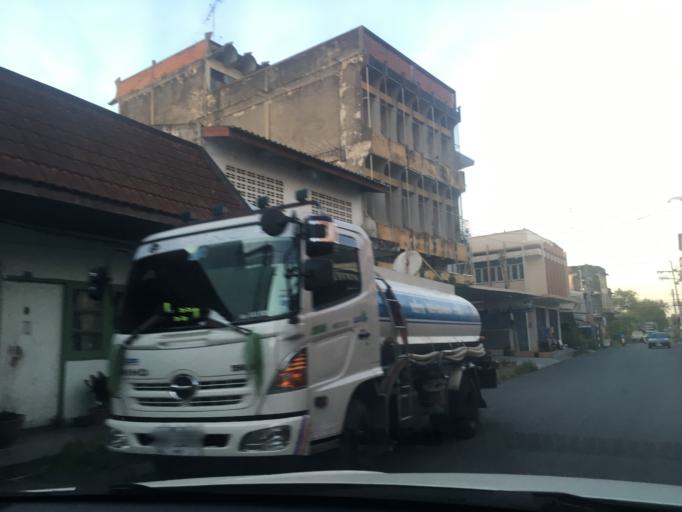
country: TH
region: Chon Buri
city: Ban Bueng
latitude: 13.3110
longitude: 101.1160
